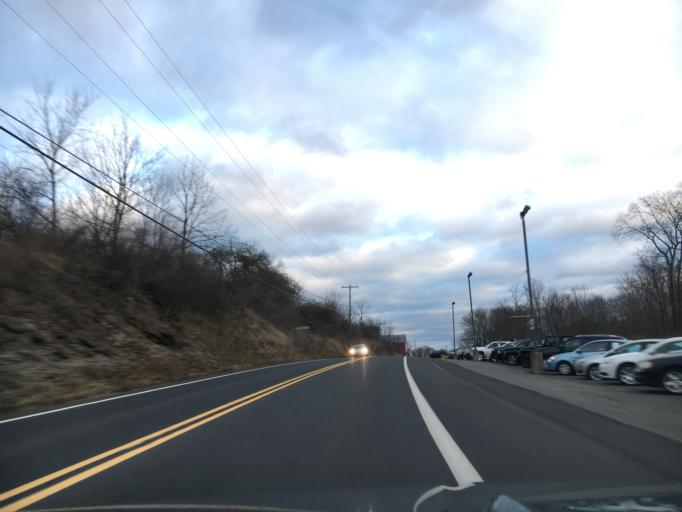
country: US
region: Pennsylvania
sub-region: Lehigh County
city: Schnecksville
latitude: 40.6858
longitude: -75.6787
